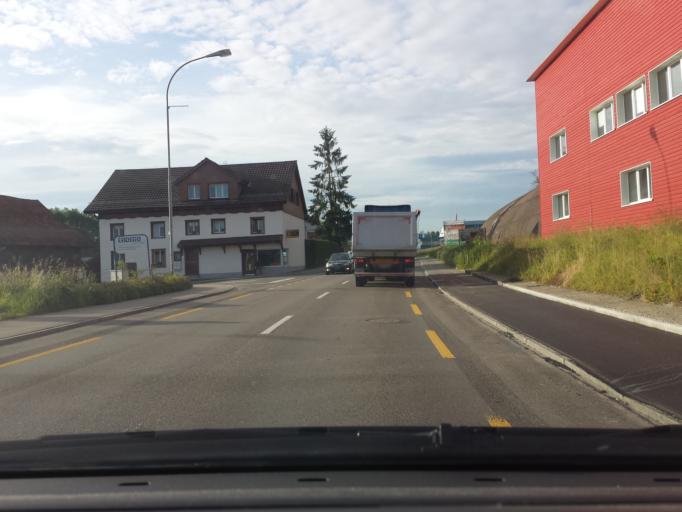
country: CH
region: Thurgau
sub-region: Arbon District
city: Egnach
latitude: 47.5473
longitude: 9.3729
